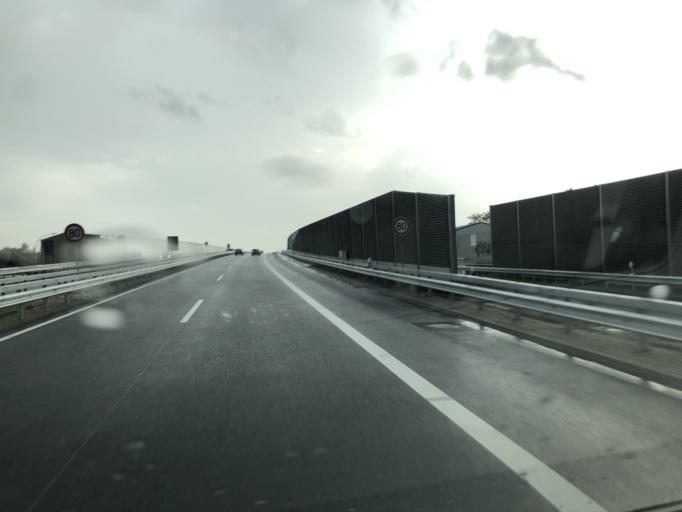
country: DE
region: Hamburg
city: Kleiner Grasbrook
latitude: 53.5077
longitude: 10.0059
